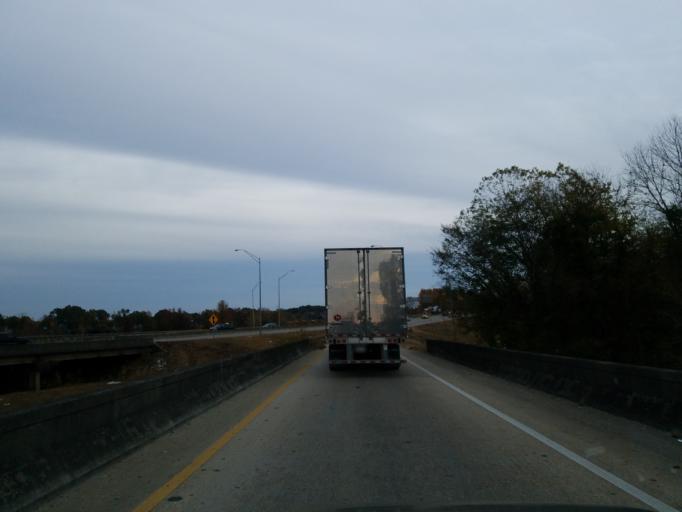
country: US
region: Mississippi
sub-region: Lauderdale County
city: Meridian
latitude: 32.3485
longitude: -88.7247
